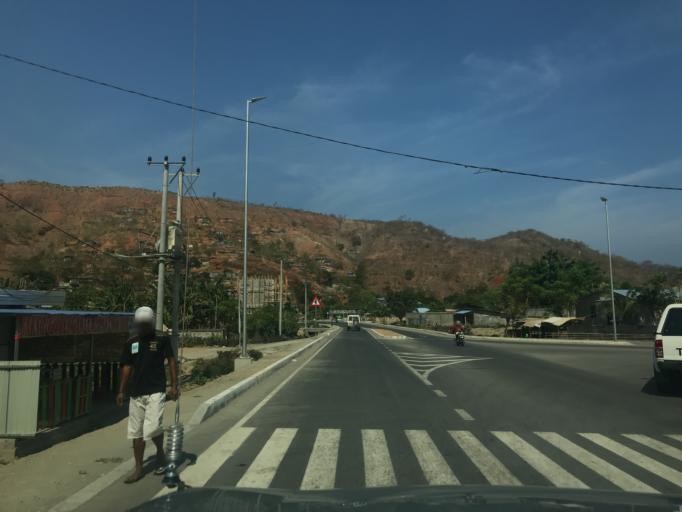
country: TL
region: Dili
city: Dili
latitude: -8.5620
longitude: 125.5264
